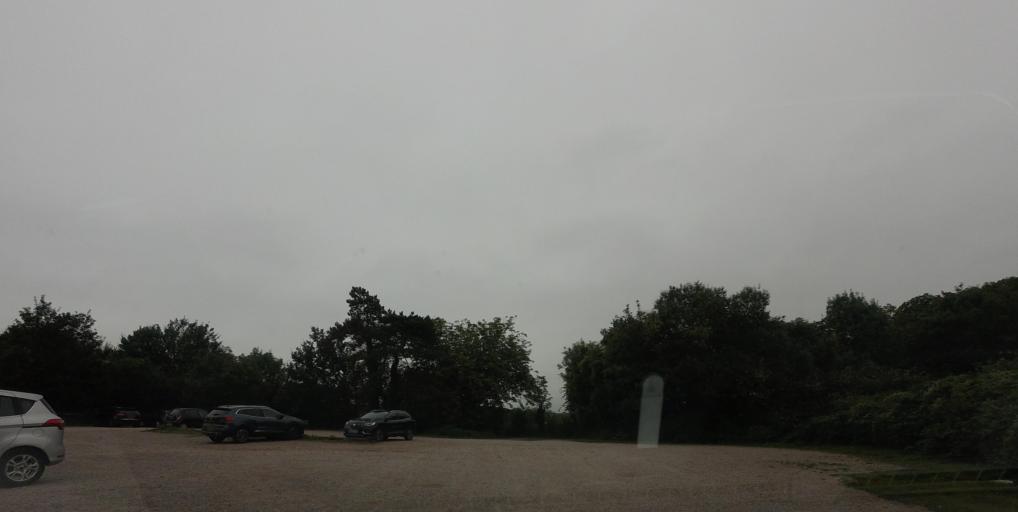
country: GB
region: England
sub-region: Kent
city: Stone
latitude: 51.4305
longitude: 0.2490
